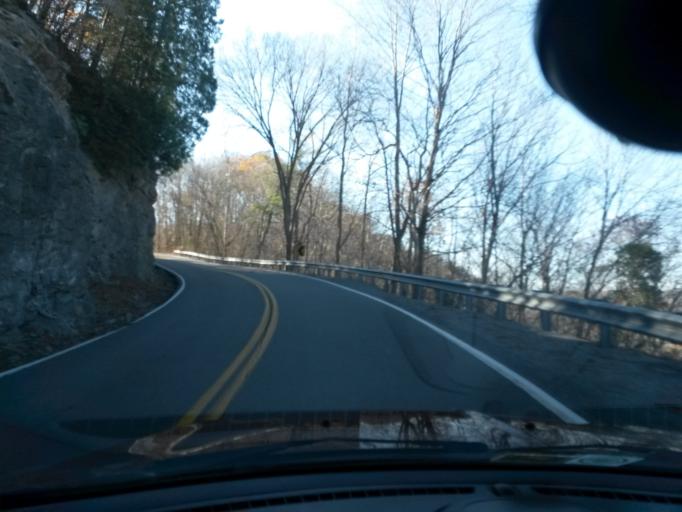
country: US
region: Virginia
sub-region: Botetourt County
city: Buchanan
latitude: 37.5815
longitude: -79.7305
